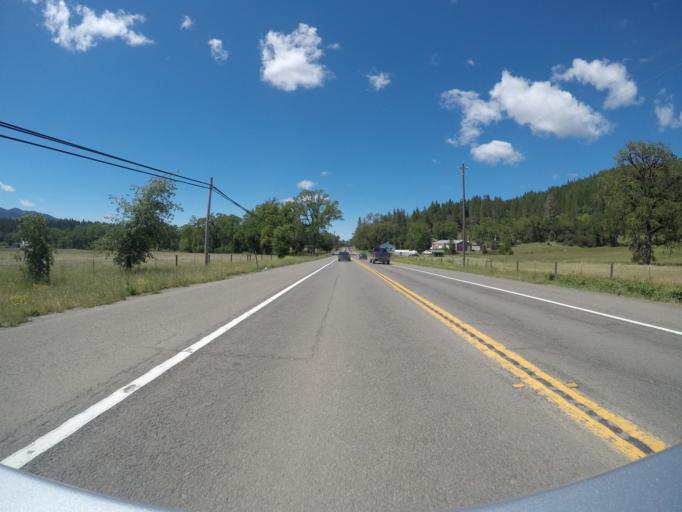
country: US
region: California
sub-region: Mendocino County
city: Laytonville
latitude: 39.6937
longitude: -123.4841
